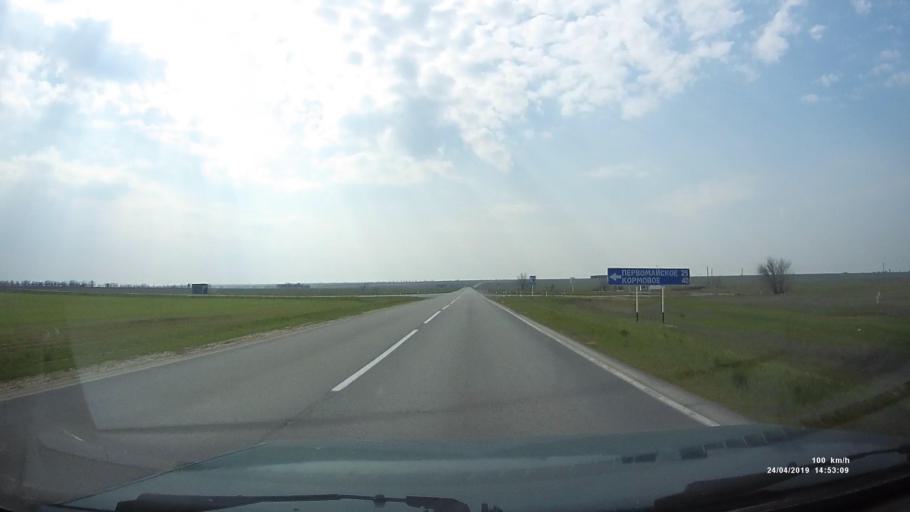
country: RU
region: Rostov
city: Remontnoye
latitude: 46.5310
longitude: 43.6651
